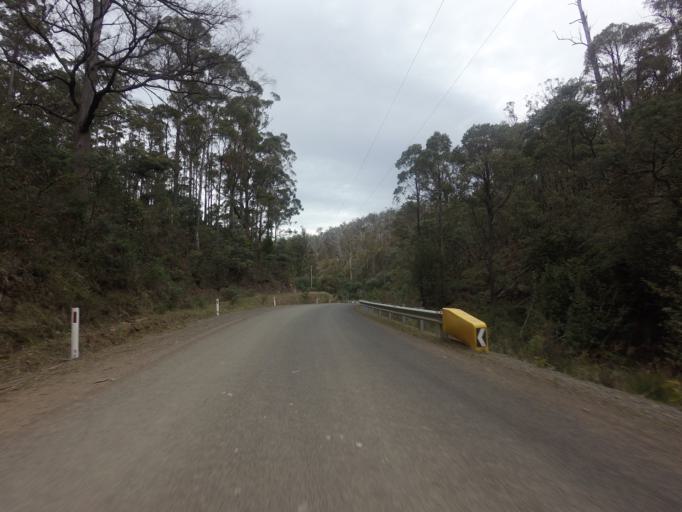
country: AU
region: Tasmania
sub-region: Derwent Valley
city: New Norfolk
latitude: -42.5853
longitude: 147.0117
